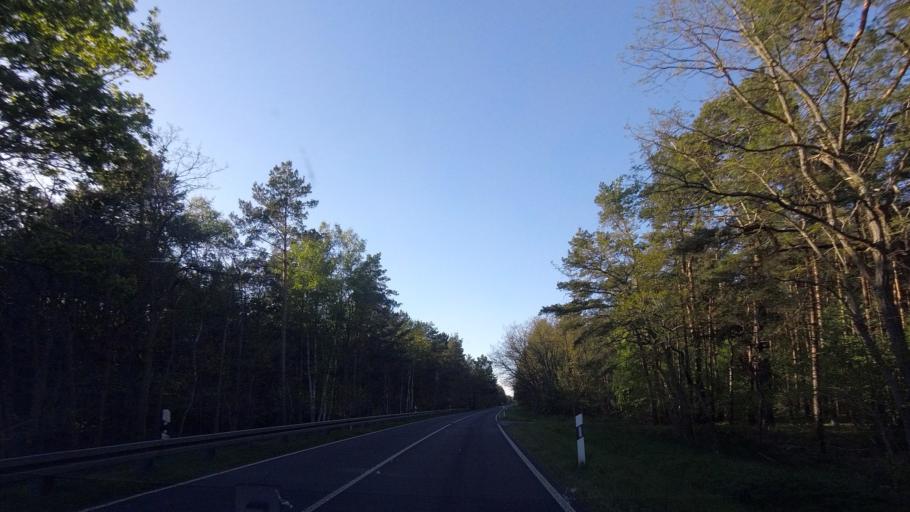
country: DE
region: Brandenburg
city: Golssen
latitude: 52.0077
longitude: 13.5525
